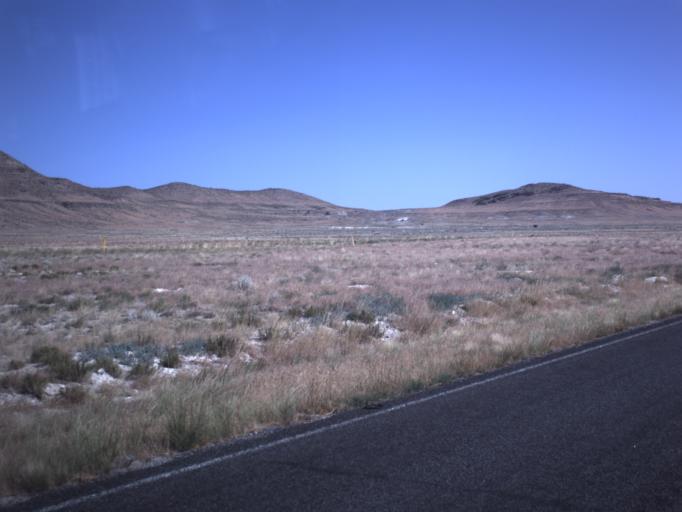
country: US
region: Utah
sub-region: Beaver County
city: Milford
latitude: 38.8565
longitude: -112.8402
